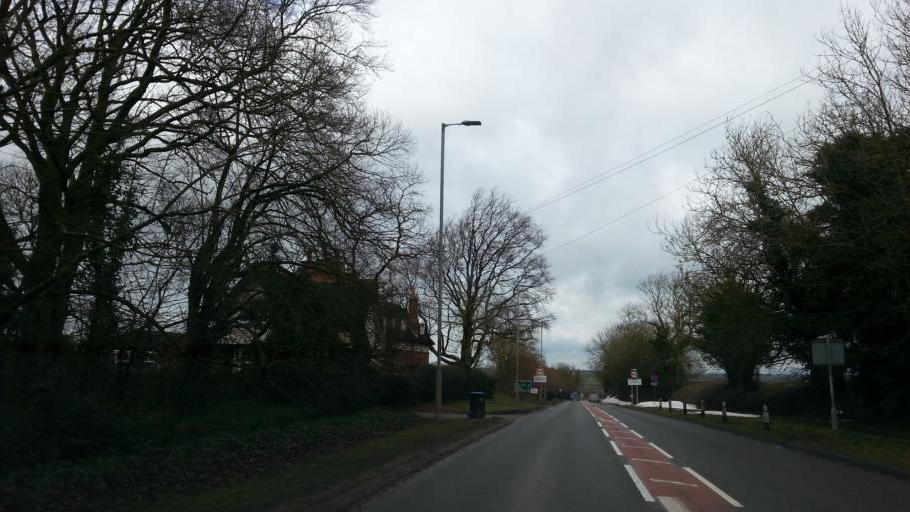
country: GB
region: England
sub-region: Leicestershire
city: Kibworth Harcourt
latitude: 52.5474
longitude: -1.0024
